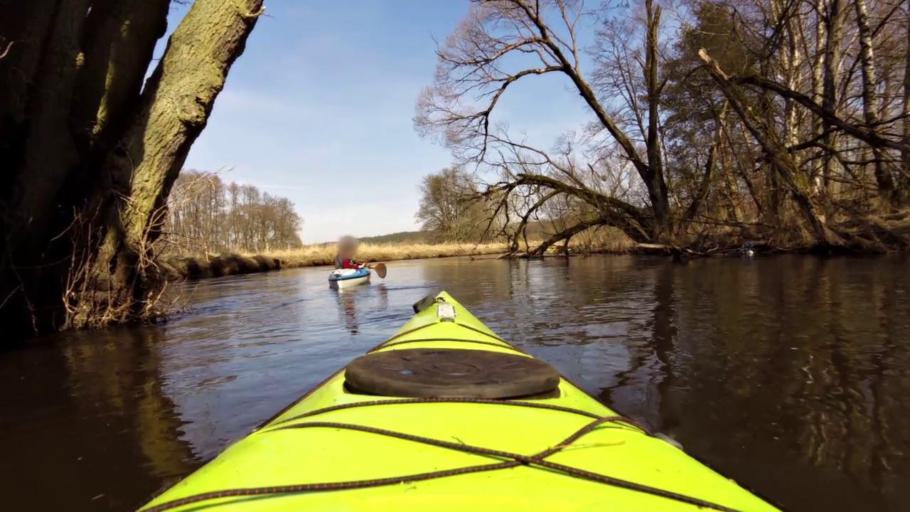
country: PL
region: West Pomeranian Voivodeship
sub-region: Powiat lobeski
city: Lobez
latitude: 53.6571
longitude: 15.5614
